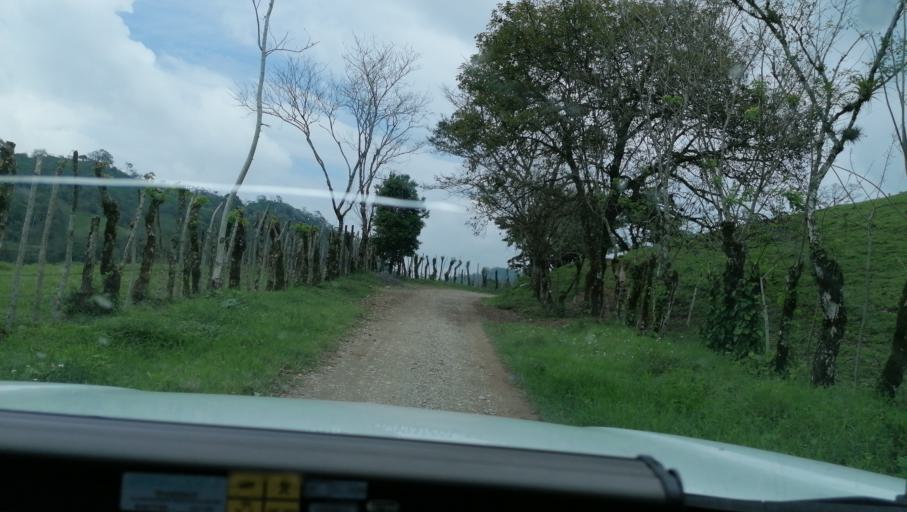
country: MX
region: Chiapas
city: Ocotepec
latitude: 17.3247
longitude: -93.1340
